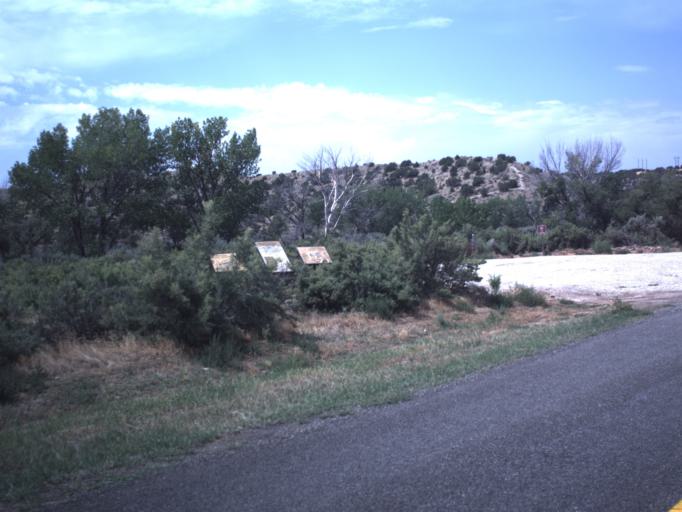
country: US
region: Utah
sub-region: Uintah County
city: Vernal
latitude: 40.5338
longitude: -109.5283
